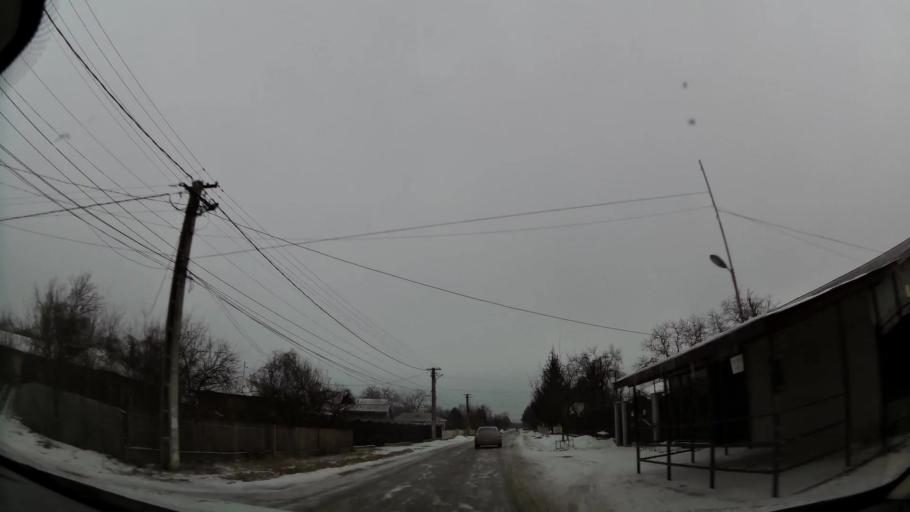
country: RO
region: Prahova
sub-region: Comuna Poenarii-Burchi
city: Ologeni
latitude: 44.7298
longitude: 25.9554
